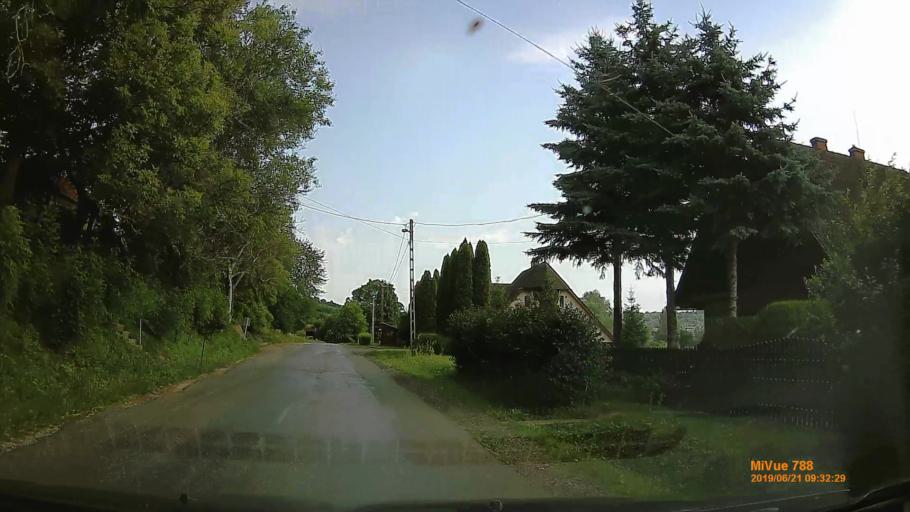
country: HU
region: Somogy
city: Taszar
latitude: 46.3124
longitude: 17.8836
